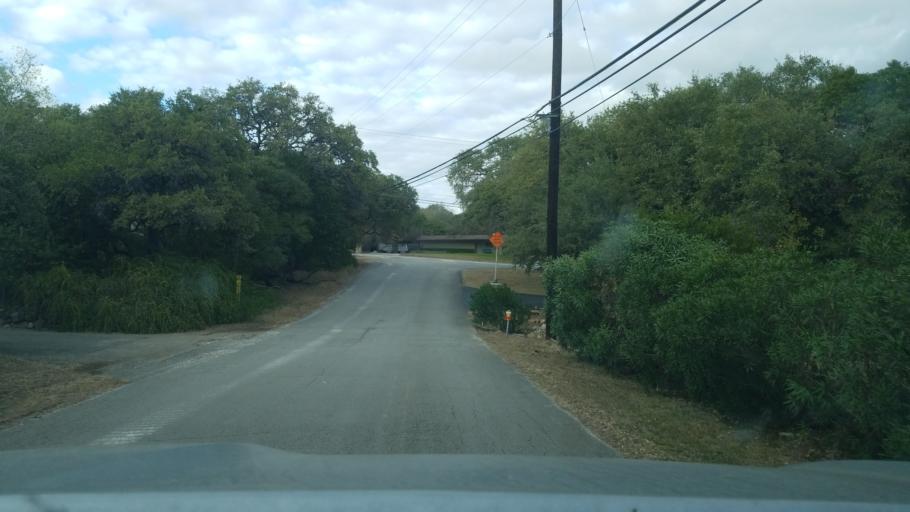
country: US
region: Texas
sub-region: Bexar County
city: Hollywood Park
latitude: 29.5989
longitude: -98.4821
